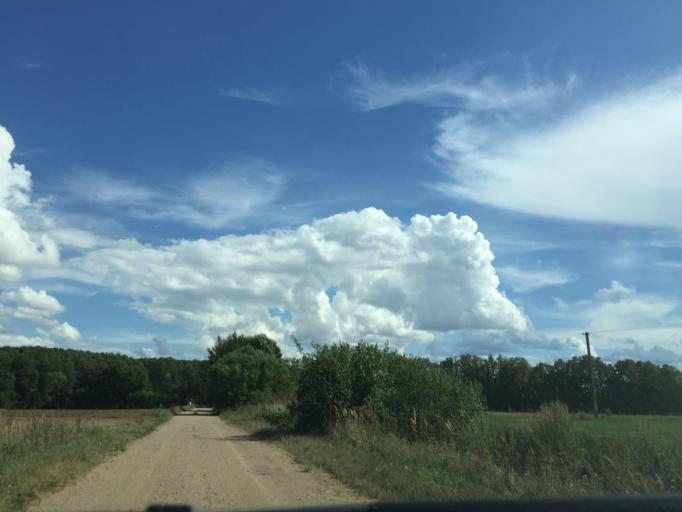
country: LT
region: Siauliu apskritis
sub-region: Joniskis
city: Joniskis
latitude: 56.3552
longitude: 23.5711
